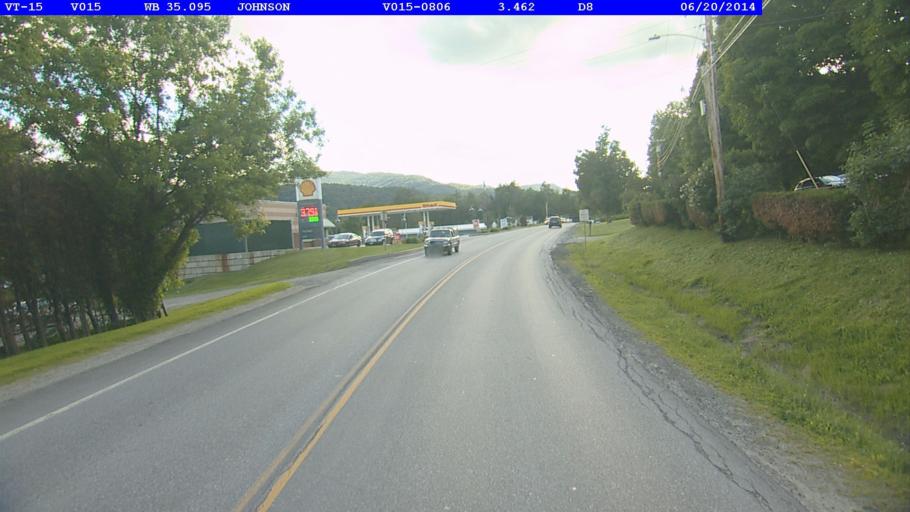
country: US
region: Vermont
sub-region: Lamoille County
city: Johnson
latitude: 44.6359
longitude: -72.6918
